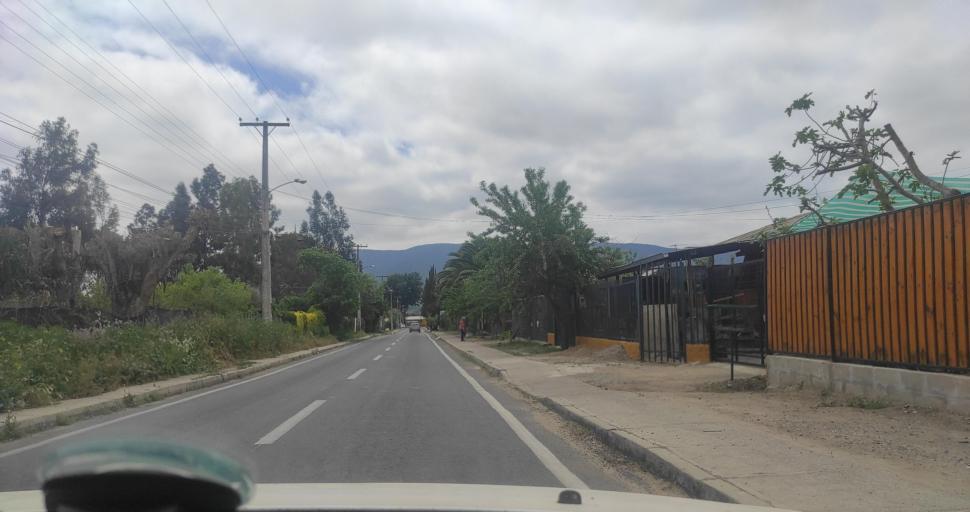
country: CL
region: Valparaiso
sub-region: Provincia de Marga Marga
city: Limache
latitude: -33.0172
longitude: -71.2427
